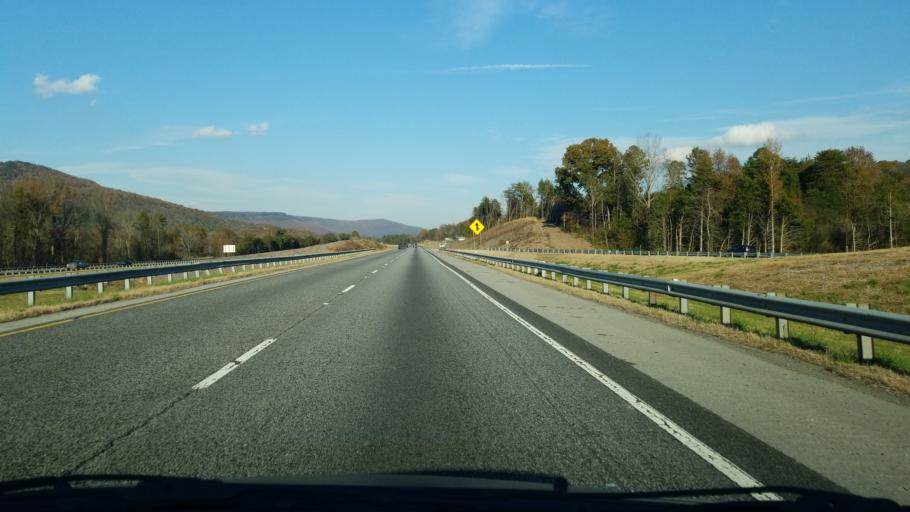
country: US
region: Georgia
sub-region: Dade County
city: Trenton
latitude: 34.9432
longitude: -85.4747
